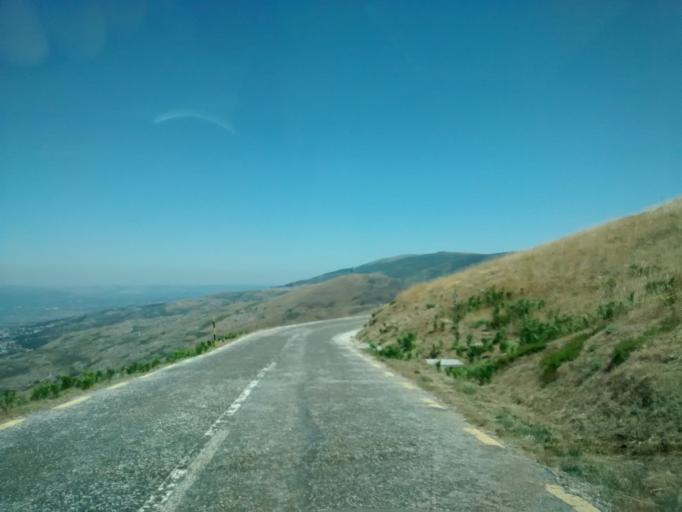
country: PT
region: Guarda
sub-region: Seia
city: Seia
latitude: 40.4233
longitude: -7.6249
